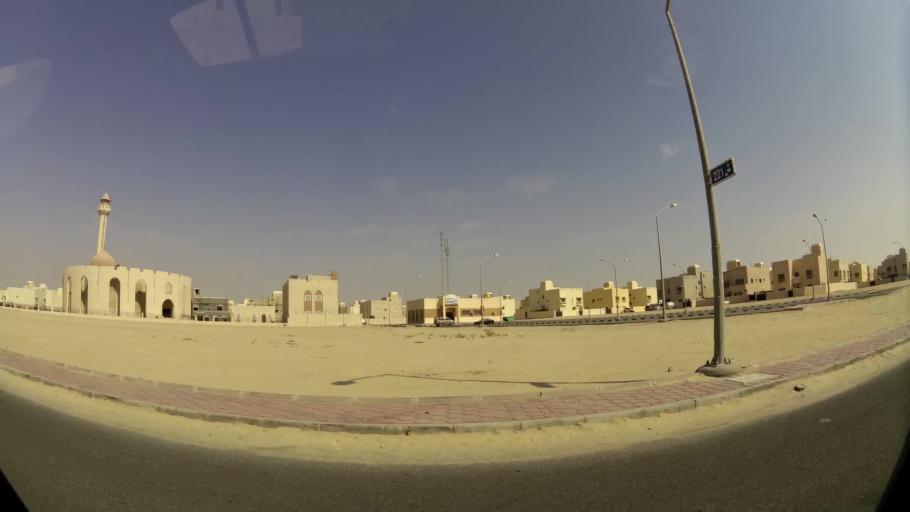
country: KW
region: Al Ahmadi
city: Al Wafrah
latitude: 28.8082
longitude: 48.0580
